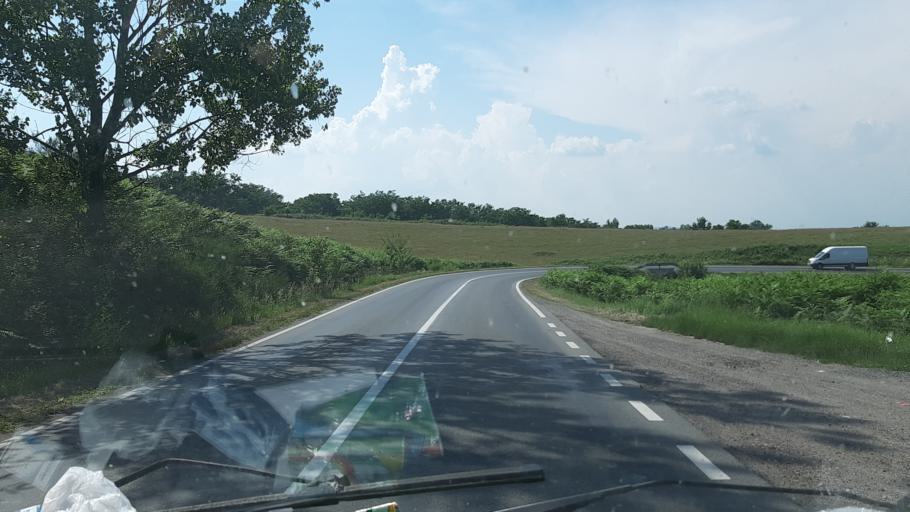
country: RO
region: Caras-Severin
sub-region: Comuna Ezeris
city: Ezeris
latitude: 45.3692
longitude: 21.9304
